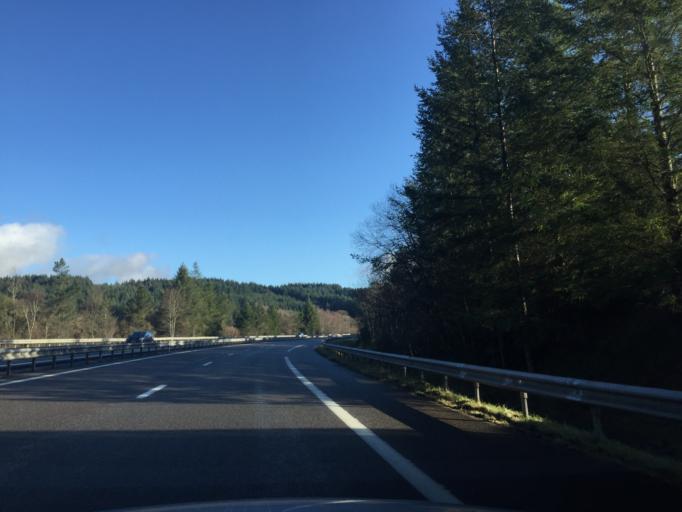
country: FR
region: Auvergne
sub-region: Departement du Puy-de-Dome
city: Chabreloche
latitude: 45.8697
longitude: 3.7098
